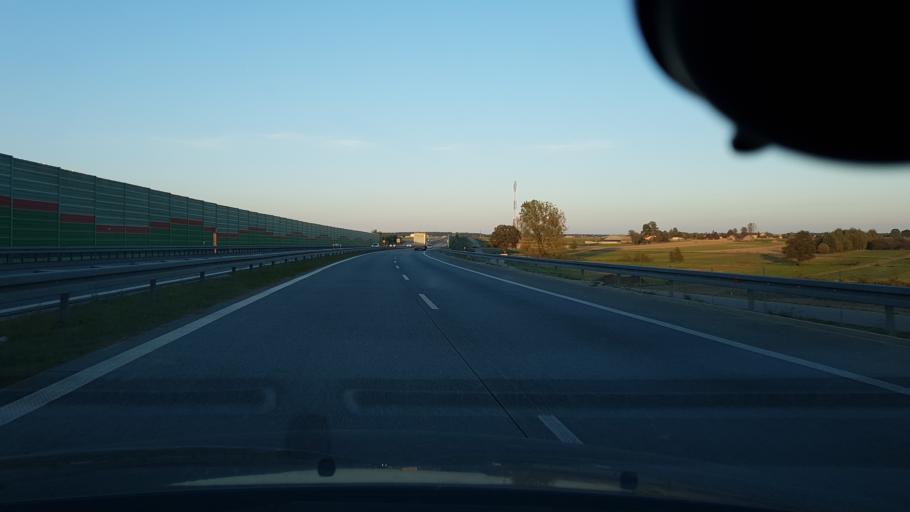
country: PL
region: Lodz Voivodeship
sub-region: Powiat tomaszowski
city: Lubochnia
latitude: 51.6097
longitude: 20.0663
